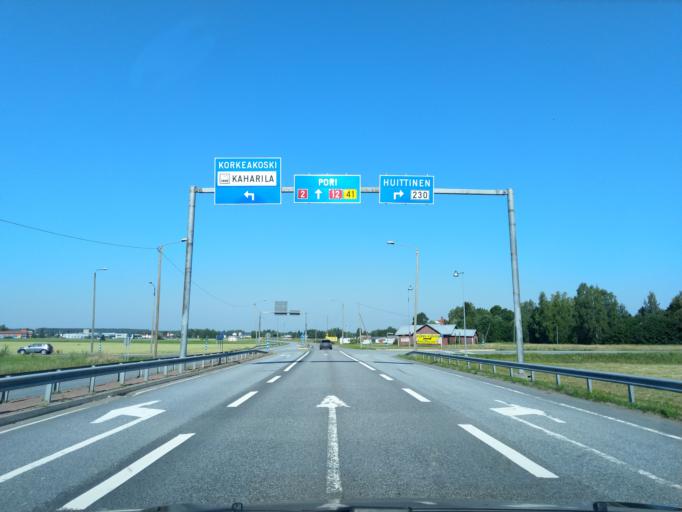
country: FI
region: Satakunta
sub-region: Pori
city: Huittinen
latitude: 61.1659
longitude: 22.7075
